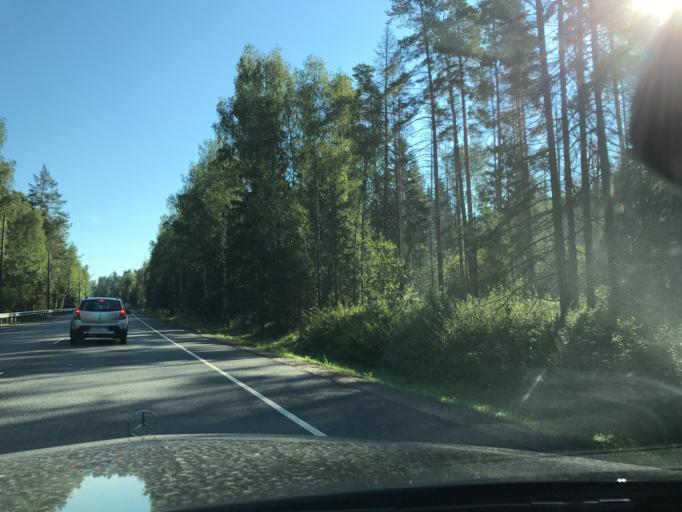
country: RU
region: Moskovskaya
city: Chernogolovka
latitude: 55.9695
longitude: 38.2925
